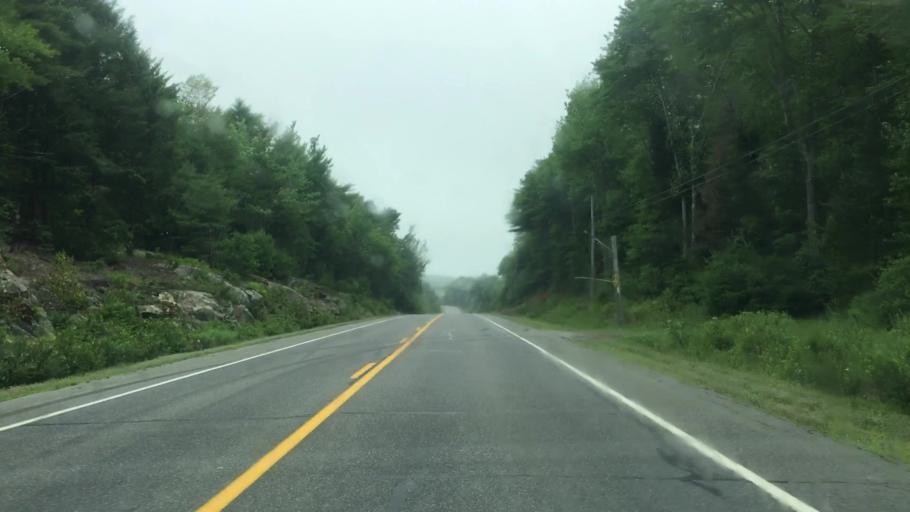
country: US
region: Maine
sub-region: Lincoln County
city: Wiscasset
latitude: 44.0823
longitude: -69.7022
